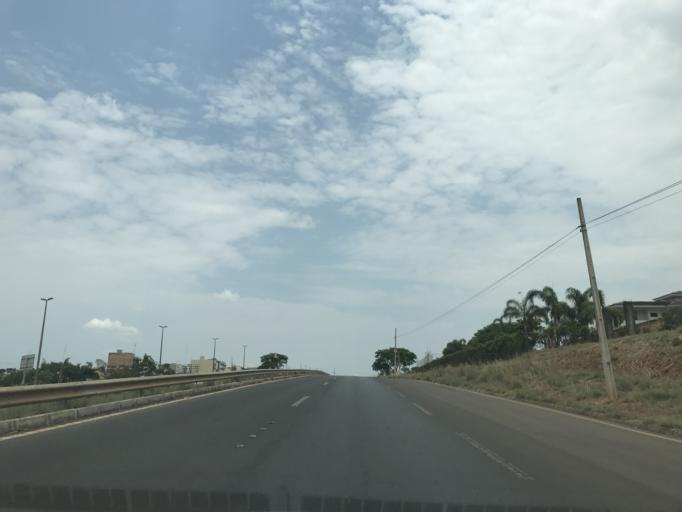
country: BR
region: Federal District
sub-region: Brasilia
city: Brasilia
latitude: -15.6788
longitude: -47.8296
